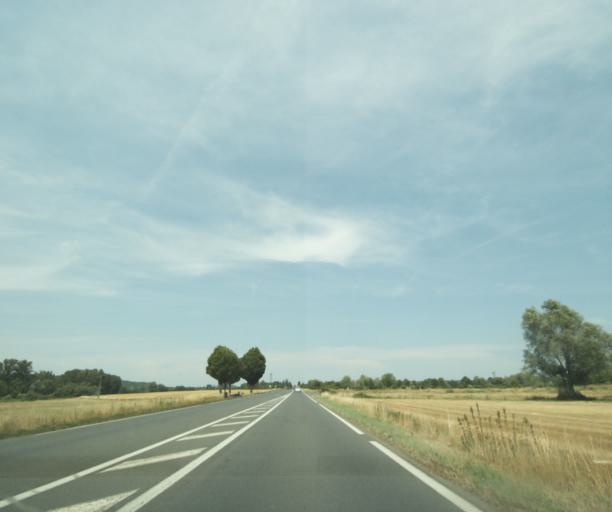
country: FR
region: Poitou-Charentes
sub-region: Departement de la Vienne
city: Antran
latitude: 46.8620
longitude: 0.5557
